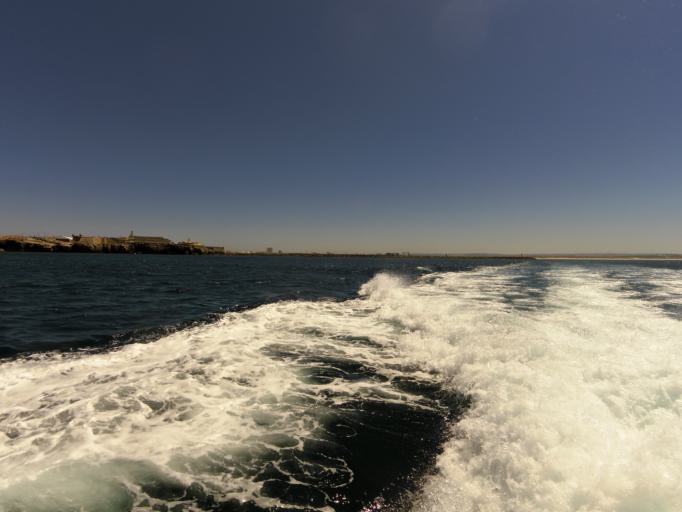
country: PT
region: Leiria
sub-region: Peniche
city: Peniche
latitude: 39.3494
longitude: -9.3856
